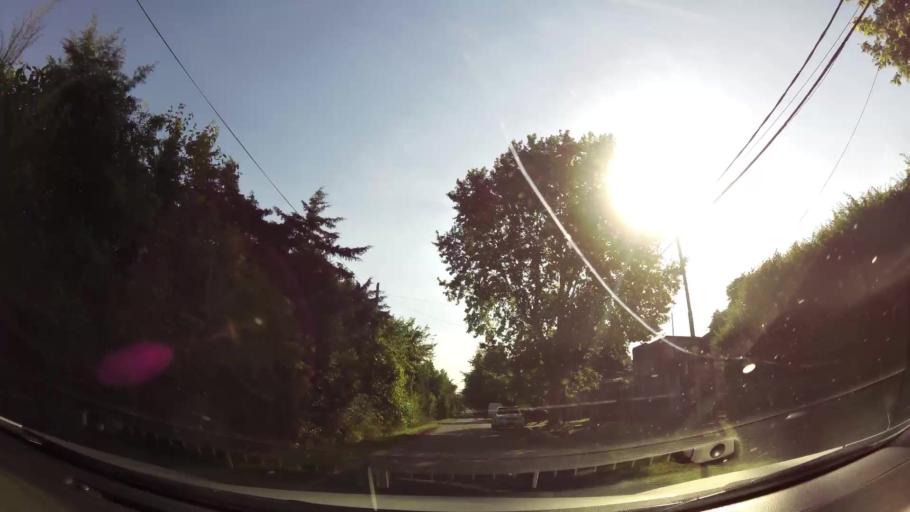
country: AR
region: Buenos Aires
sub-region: Partido de Tigre
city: Tigre
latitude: -34.4737
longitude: -58.6376
